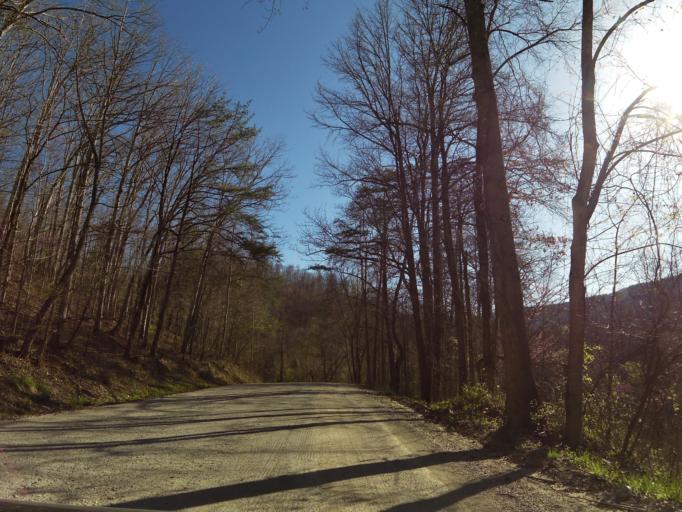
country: US
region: Tennessee
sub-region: Scott County
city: Huntsville
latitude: 36.3167
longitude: -84.3783
